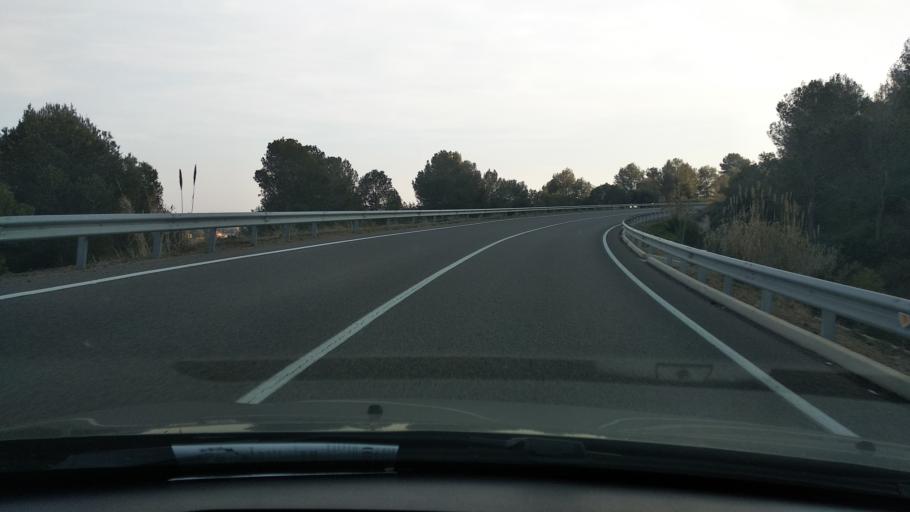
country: ES
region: Catalonia
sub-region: Provincia de Tarragona
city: les Borges del Camp
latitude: 41.1779
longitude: 1.0104
